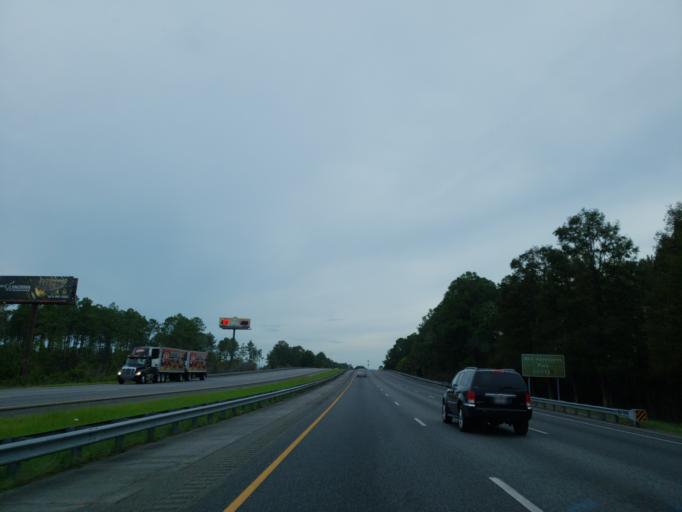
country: US
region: Georgia
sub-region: Lowndes County
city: Valdosta
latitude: 30.7564
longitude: -83.2786
